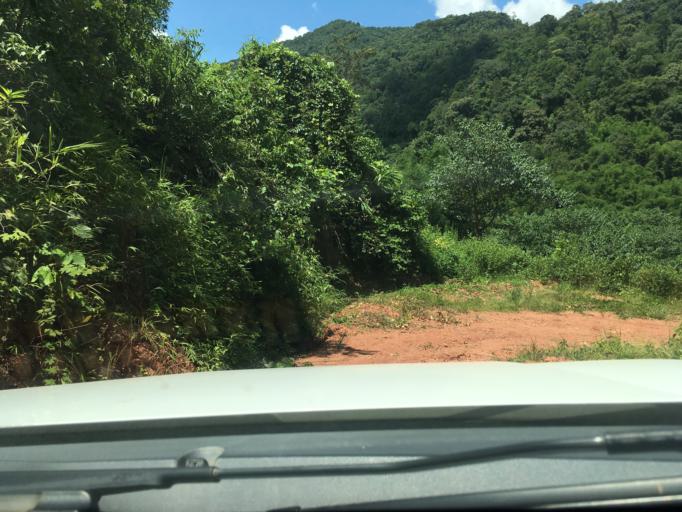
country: LA
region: Phongsali
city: Phongsali
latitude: 21.7897
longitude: 101.8659
